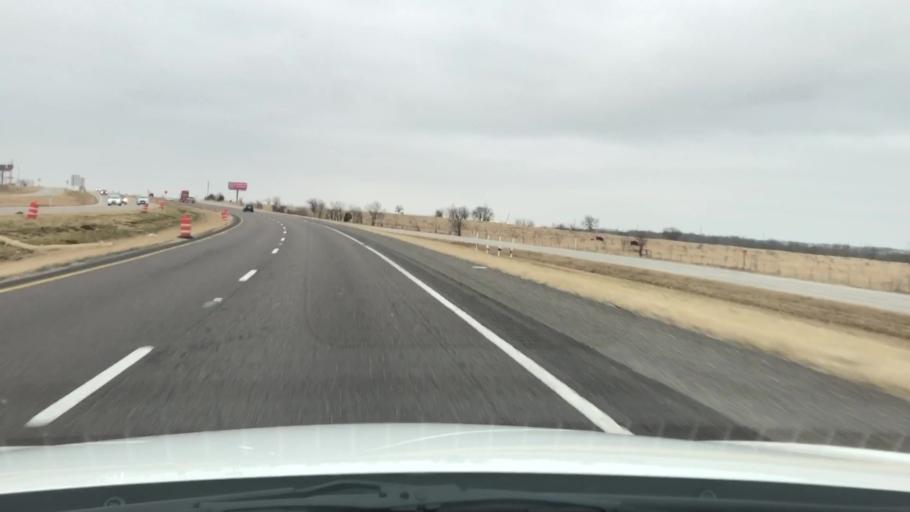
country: US
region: Texas
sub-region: Cooke County
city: Gainesville
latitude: 33.6717
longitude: -97.1509
